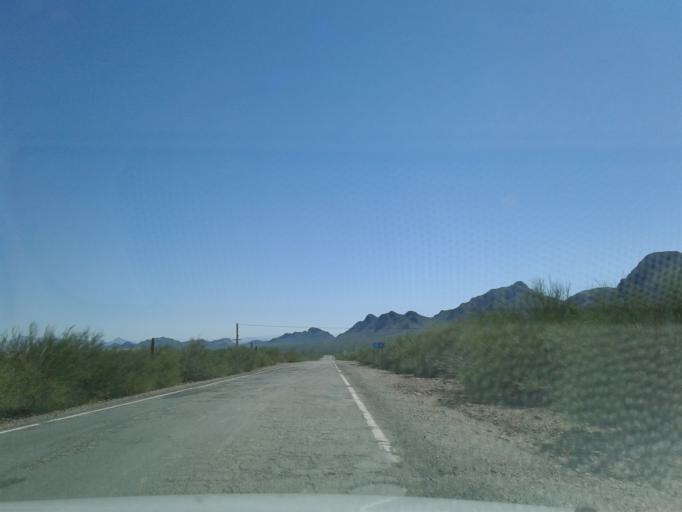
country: US
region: Arizona
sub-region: Pima County
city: Avra Valley
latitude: 32.3854
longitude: -111.4955
